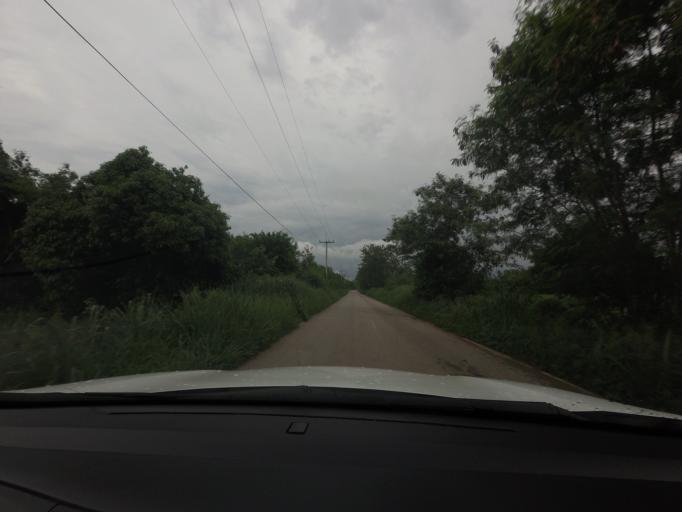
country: TH
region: Nakhon Ratchasima
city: Pak Chong
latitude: 14.6561
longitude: 101.4199
